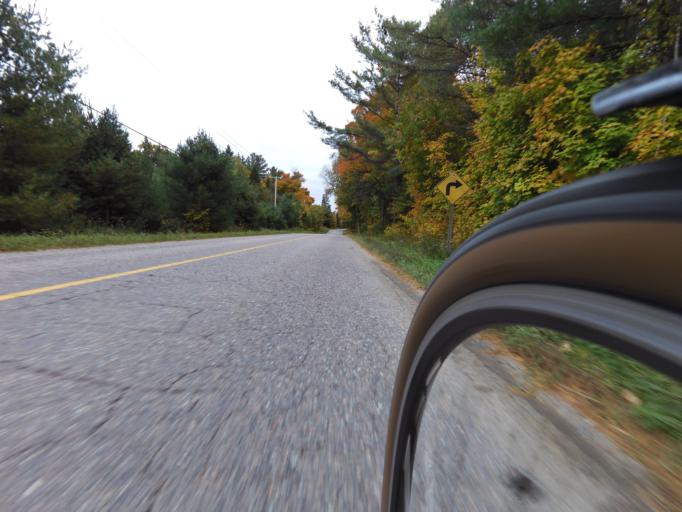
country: CA
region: Quebec
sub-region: Outaouais
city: Wakefield
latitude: 45.6738
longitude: -76.0098
